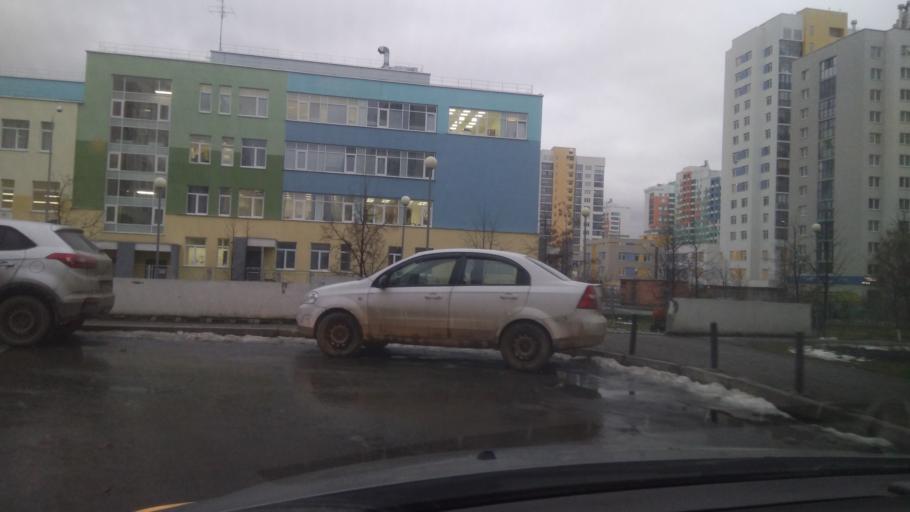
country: RU
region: Sverdlovsk
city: Shirokaya Rechka
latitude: 56.7893
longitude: 60.5186
